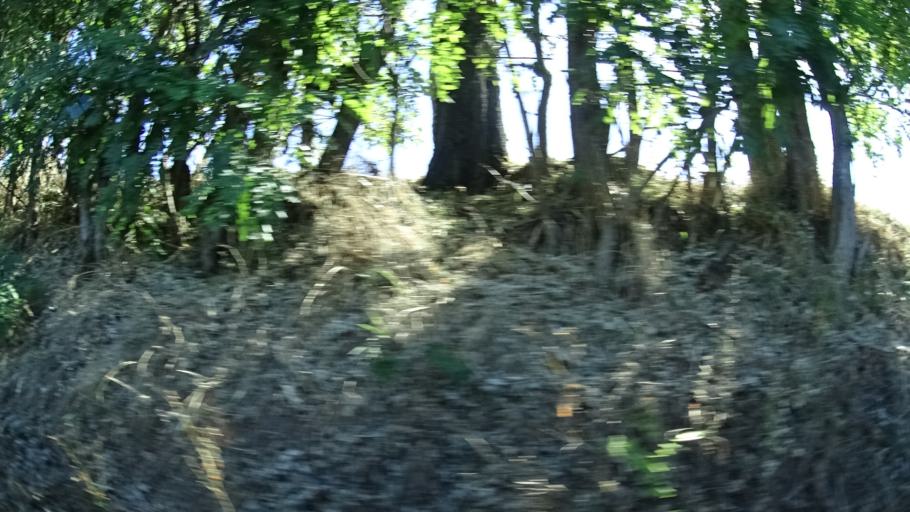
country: DE
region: Baden-Wuerttemberg
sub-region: Karlsruhe Region
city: Ubstadt-Weiher
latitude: 49.1269
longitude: 8.6480
